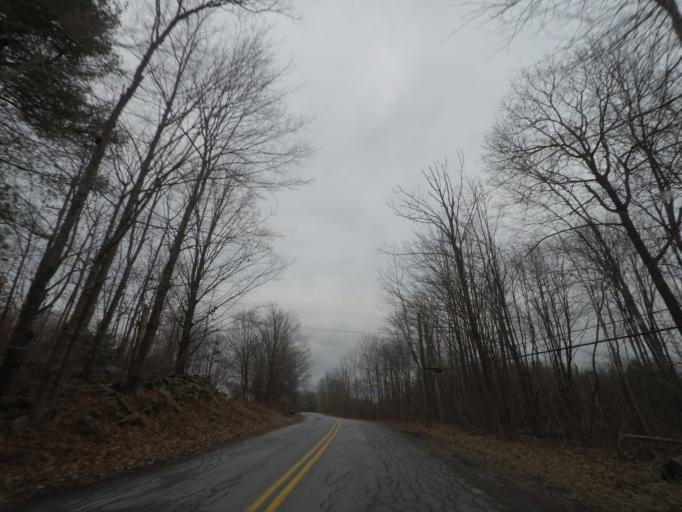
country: US
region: New York
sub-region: Rensselaer County
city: Poestenkill
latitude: 42.7648
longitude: -73.4963
